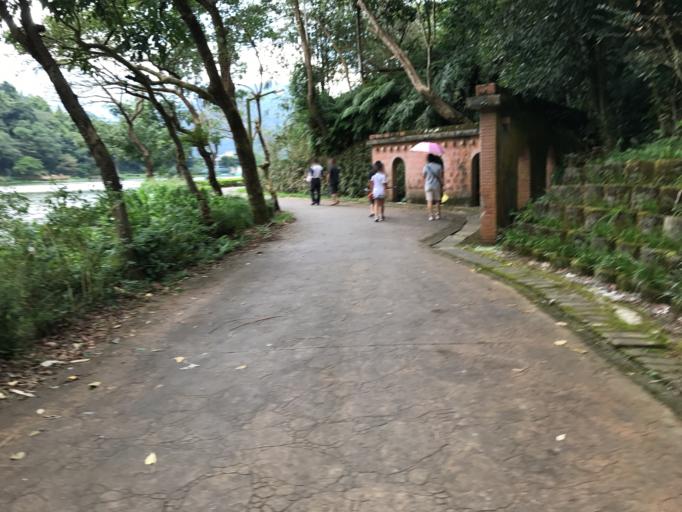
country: TW
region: Taiwan
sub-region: Nantou
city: Puli
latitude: 23.9584
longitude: 120.9963
